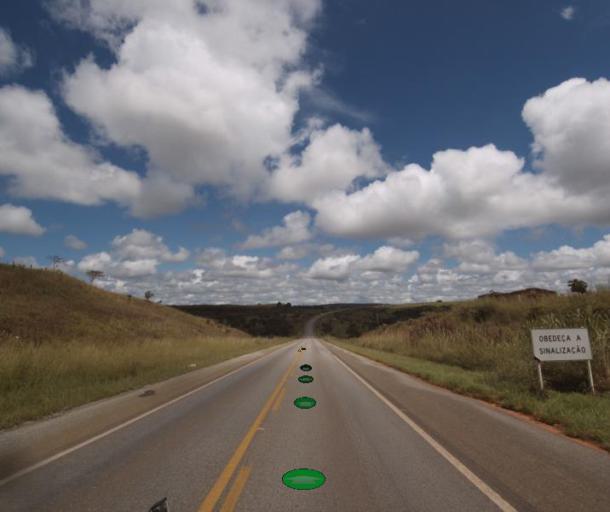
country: BR
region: Goias
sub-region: Abadiania
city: Abadiania
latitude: -15.7775
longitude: -48.4704
